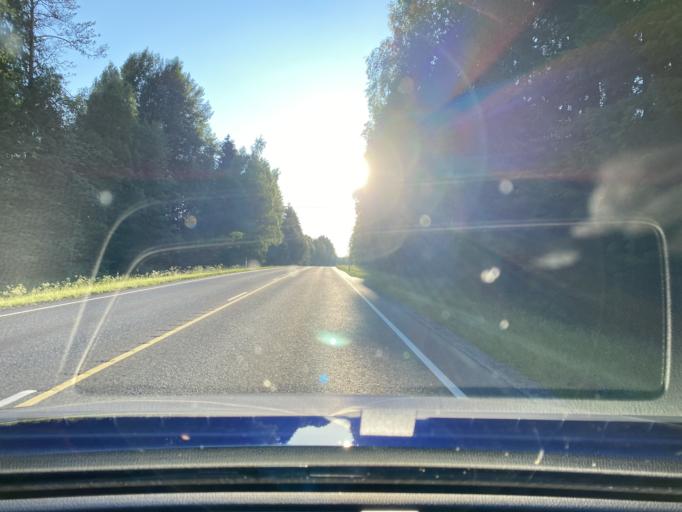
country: FI
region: Haeme
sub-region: Haemeenlinna
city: Renko
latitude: 60.7914
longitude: 24.1179
